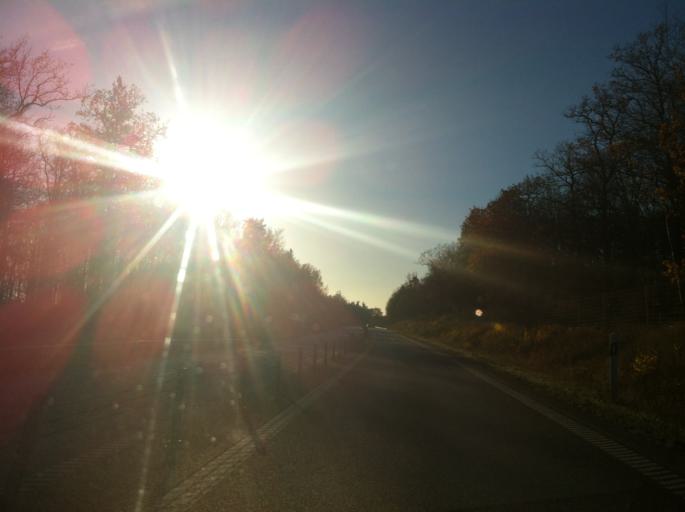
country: SE
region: Blekinge
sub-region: Karlshamns Kommun
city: Morrum
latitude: 56.1880
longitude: 14.7858
